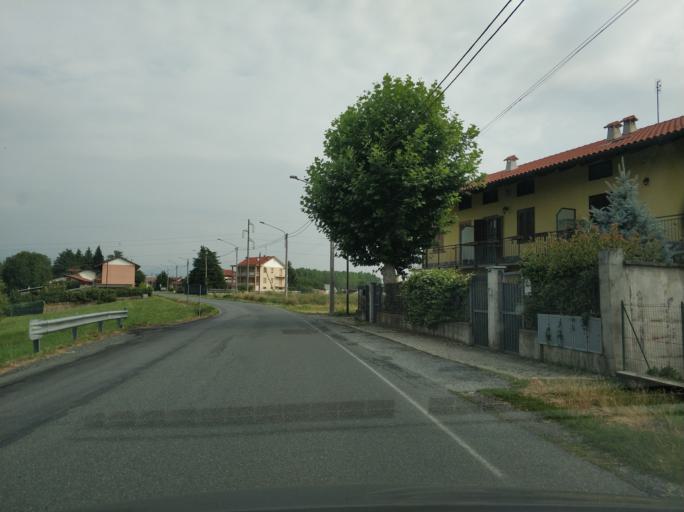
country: IT
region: Piedmont
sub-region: Provincia di Torino
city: Cirie
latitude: 45.2070
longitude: 7.5976
